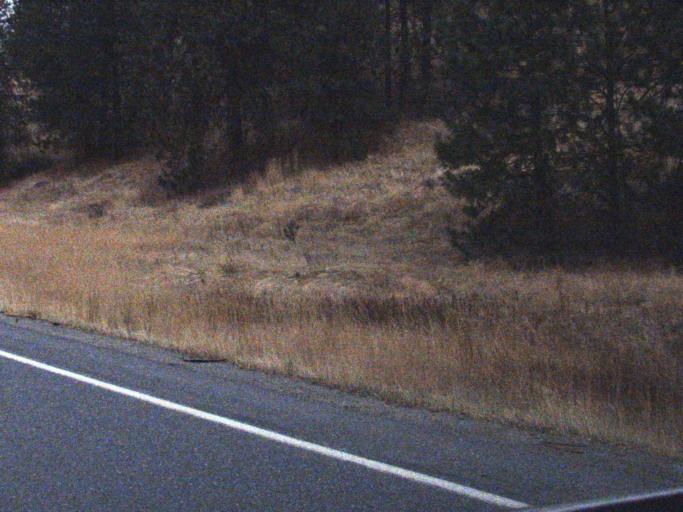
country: US
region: Washington
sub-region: Stevens County
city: Kettle Falls
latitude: 48.5930
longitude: -117.9980
